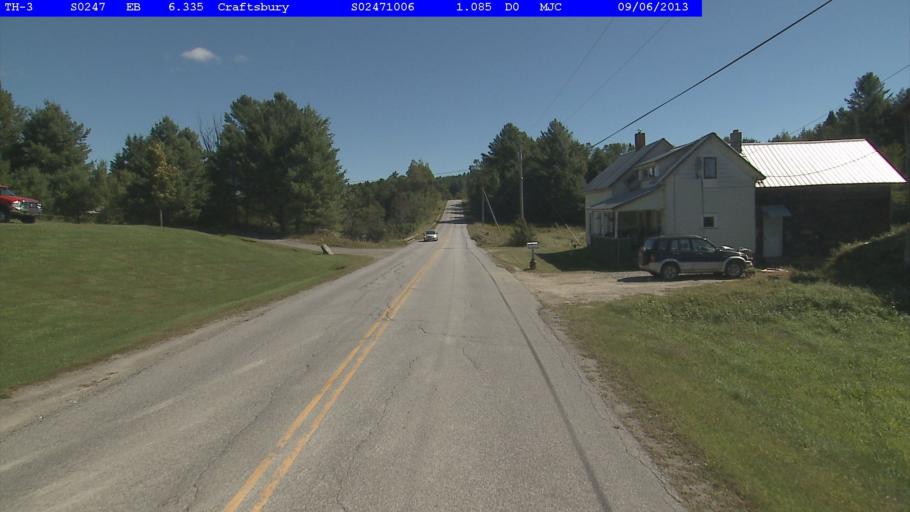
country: US
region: Vermont
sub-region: Caledonia County
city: Hardwick
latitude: 44.6310
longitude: -72.4292
